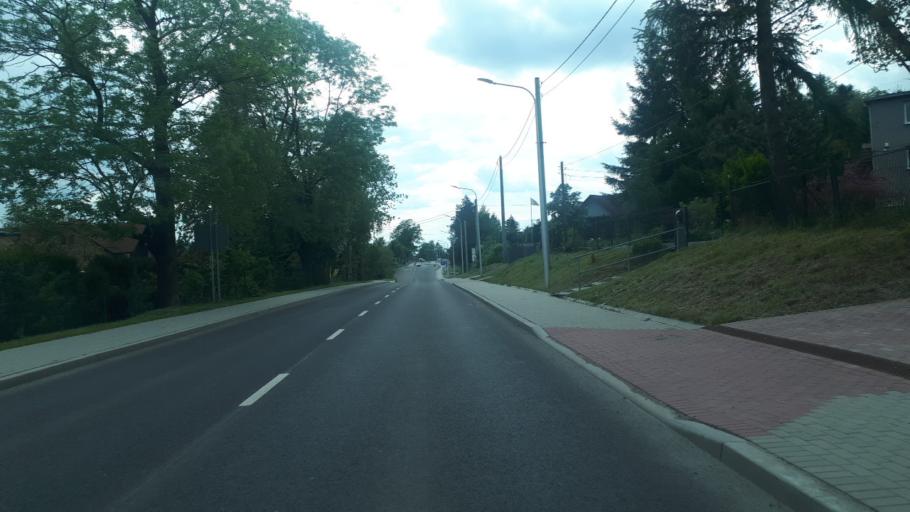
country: PL
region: Silesian Voivodeship
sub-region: Bielsko-Biala
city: Bielsko-Biala
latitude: 49.8222
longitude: 19.0794
